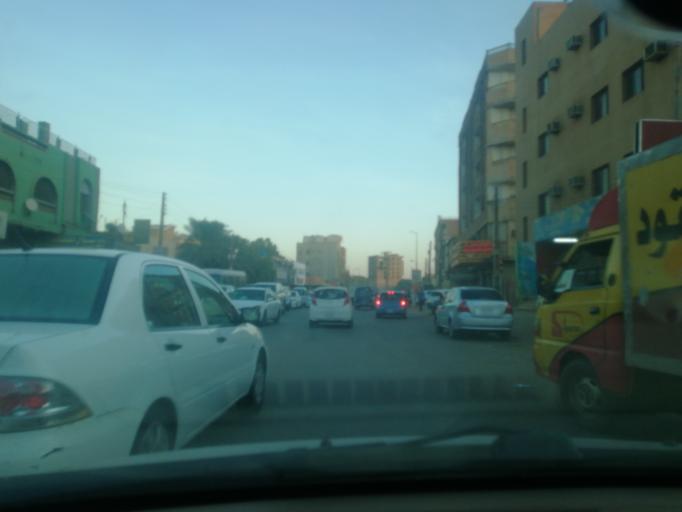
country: SD
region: Khartoum
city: Khartoum
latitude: 15.6238
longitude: 32.5567
